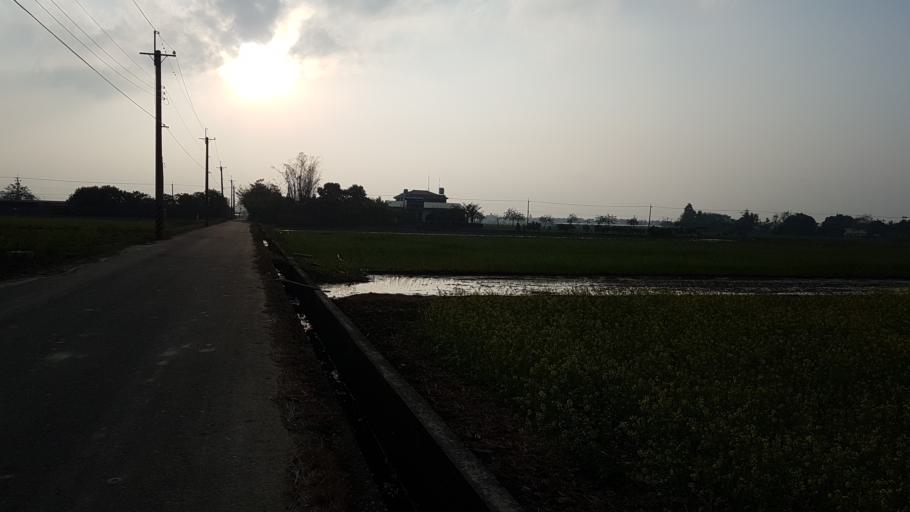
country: TW
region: Taiwan
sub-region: Chiayi
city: Jiayi Shi
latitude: 23.3702
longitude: 120.4530
